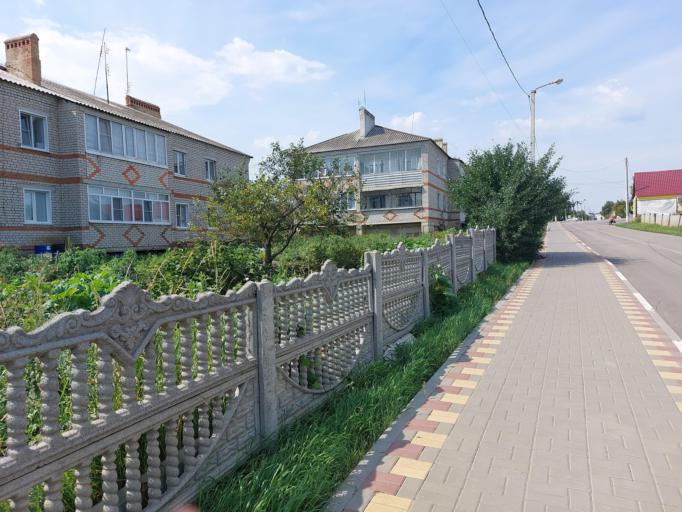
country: RU
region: Lipetsk
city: Dolgorukovo
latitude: 52.3261
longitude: 38.3636
